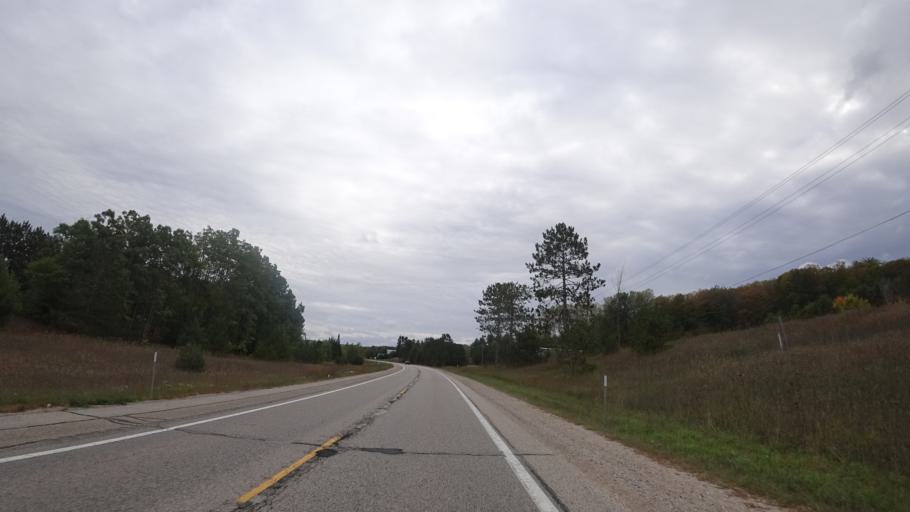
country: US
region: Michigan
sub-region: Charlevoix County
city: Boyne City
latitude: 45.2026
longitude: -84.9246
